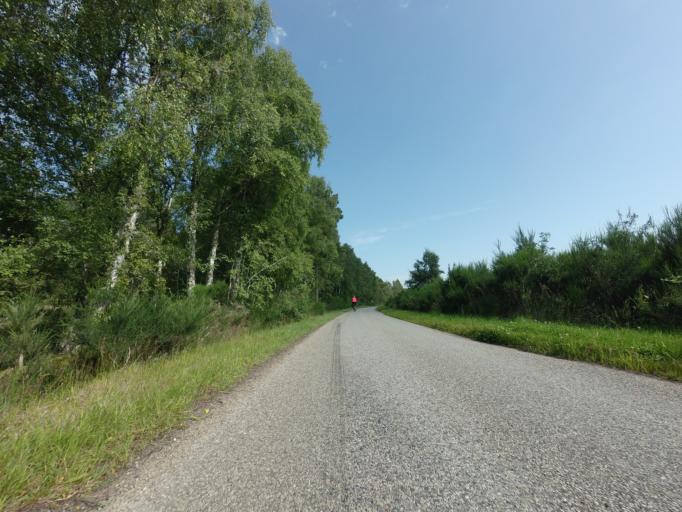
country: GB
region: Scotland
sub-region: Highland
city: Invergordon
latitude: 57.7341
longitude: -4.1908
